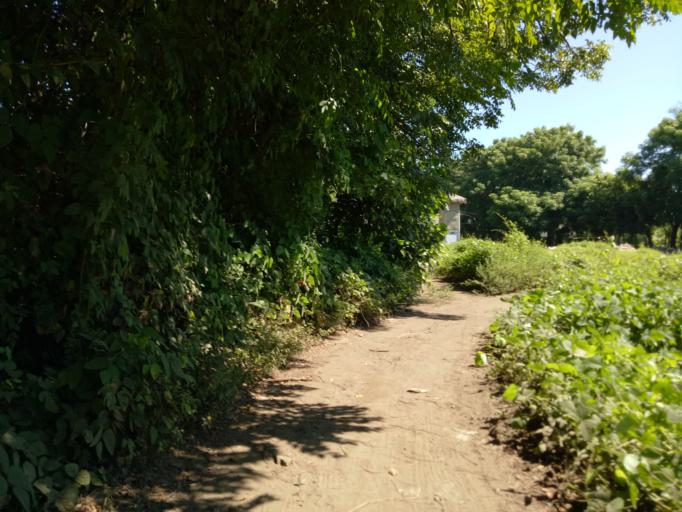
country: ID
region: West Nusa Tenggara
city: Gili Air
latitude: -8.3547
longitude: 116.0812
